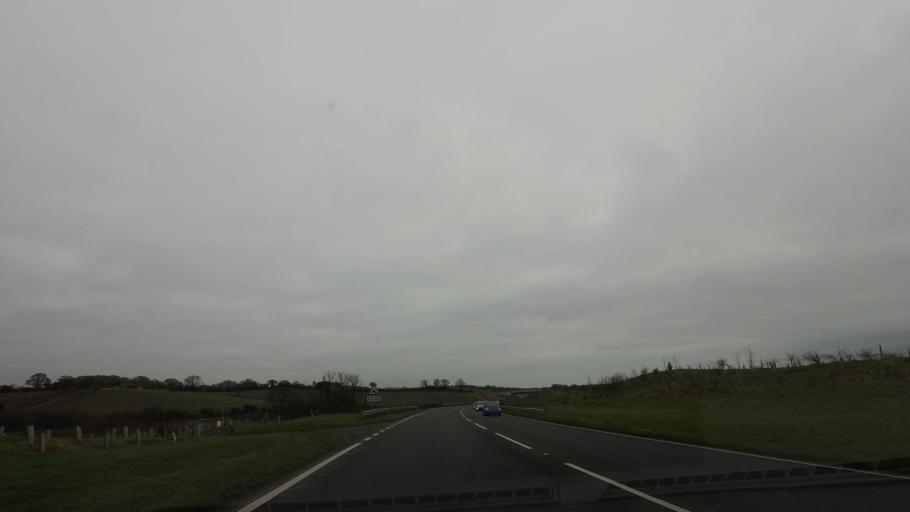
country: GB
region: England
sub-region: East Sussex
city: Bexhill-on-Sea
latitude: 50.8682
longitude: 0.4884
